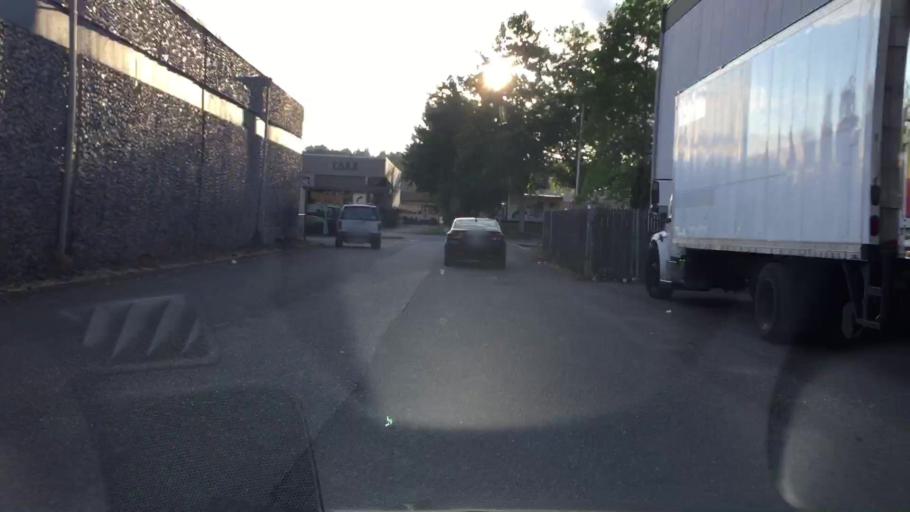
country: US
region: Washington
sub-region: King County
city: Tukwila
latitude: 47.4466
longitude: -122.2499
